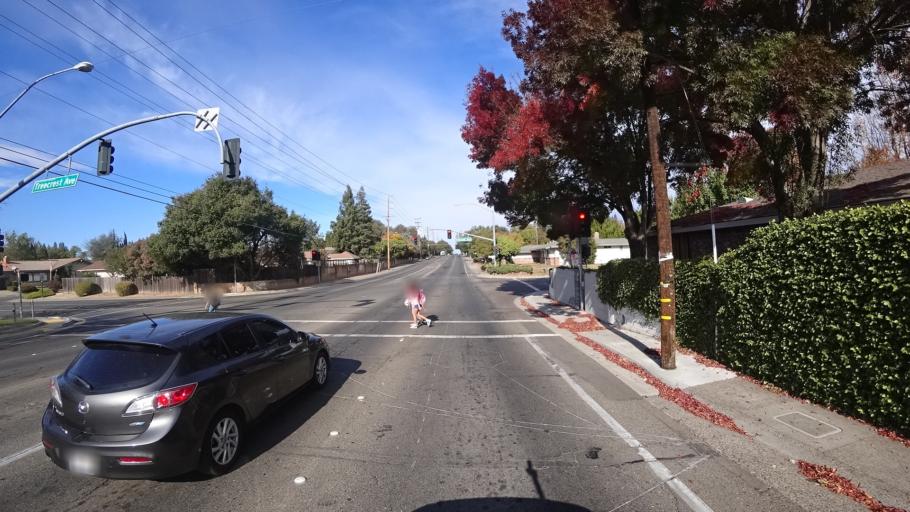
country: US
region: California
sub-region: Sacramento County
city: Fair Oaks
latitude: 38.6682
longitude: -121.2622
